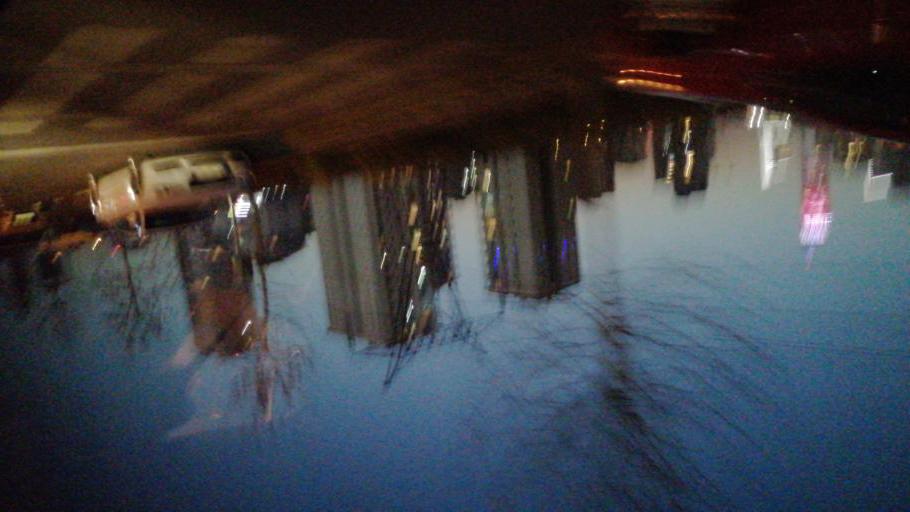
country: TR
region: Istanbul
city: Umraniye
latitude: 41.0022
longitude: 29.1377
